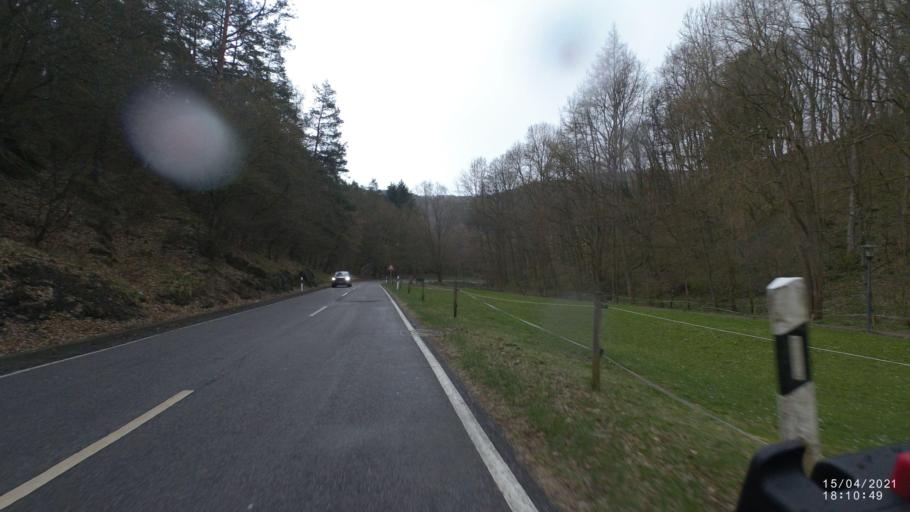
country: DE
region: Rheinland-Pfalz
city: Volkesfeld
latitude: 50.3868
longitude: 7.1493
